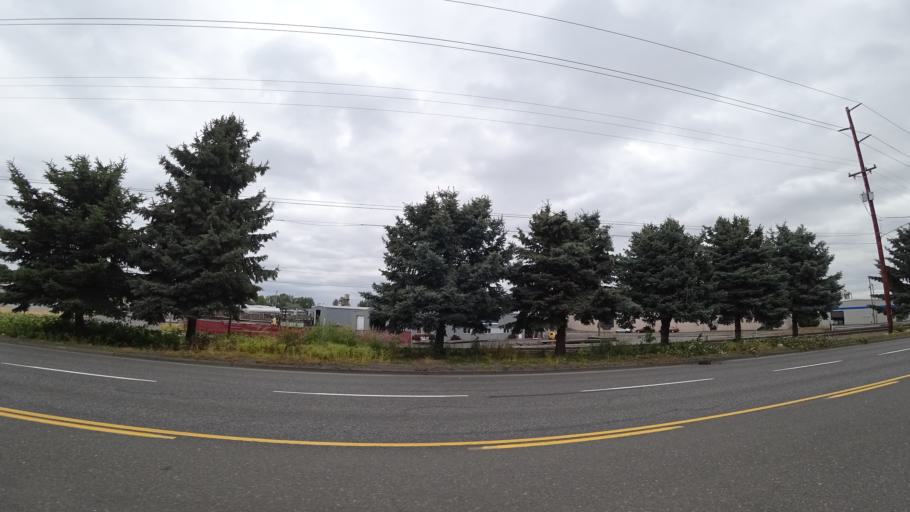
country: US
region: Washington
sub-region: Clark County
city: Vancouver
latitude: 45.5880
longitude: -122.6951
